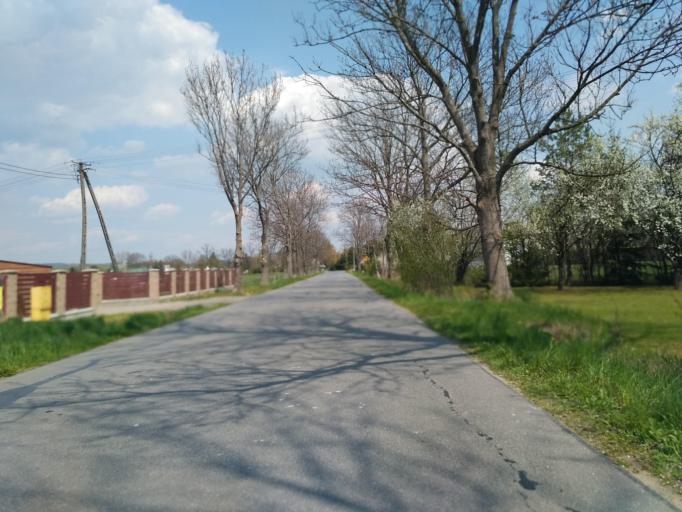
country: PL
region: Subcarpathian Voivodeship
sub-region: Powiat jasielski
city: Tarnowiec
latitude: 49.7413
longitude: 21.5449
